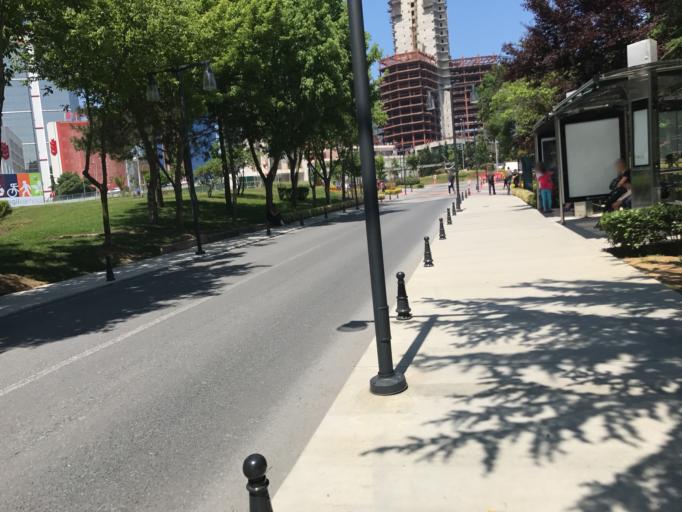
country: TR
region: Istanbul
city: Sisli
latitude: 41.1073
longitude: 29.0219
